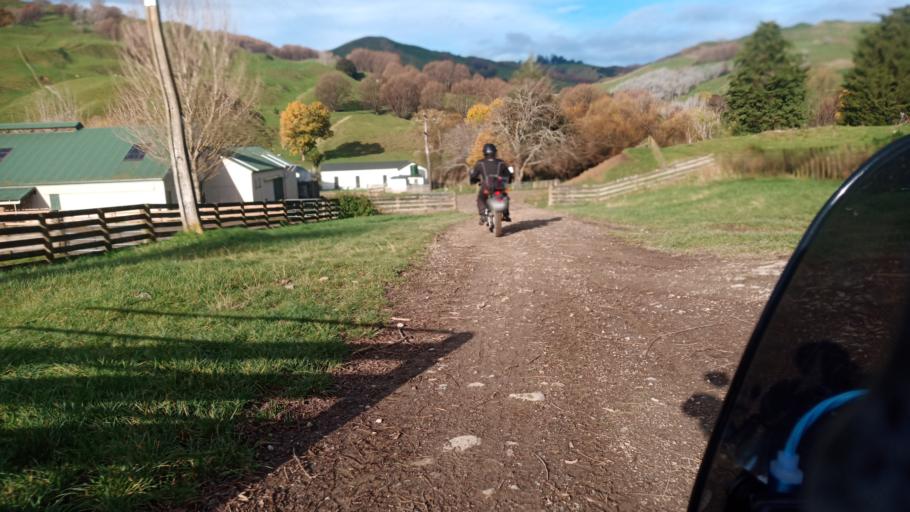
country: NZ
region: Gisborne
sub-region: Gisborne District
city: Gisborne
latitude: -38.3487
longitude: 177.9388
